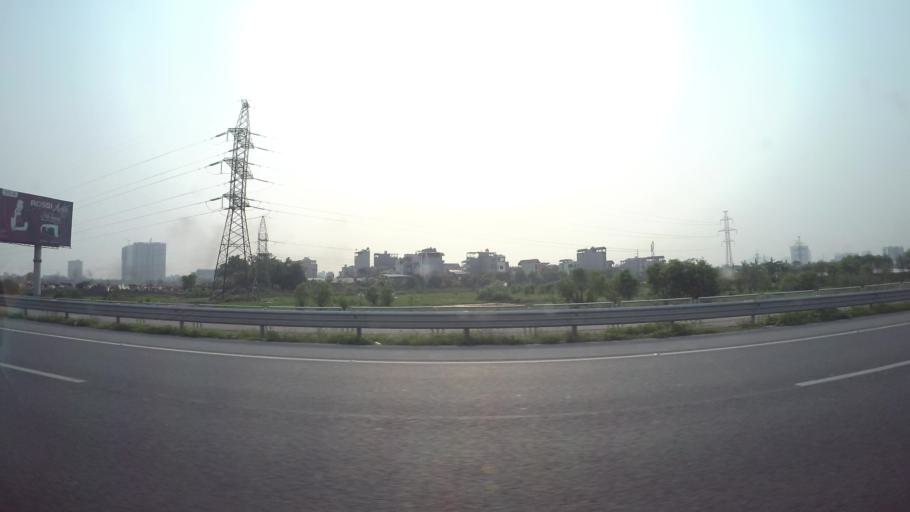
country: VN
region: Ha Noi
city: Van Dien
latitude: 20.9402
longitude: 105.8593
